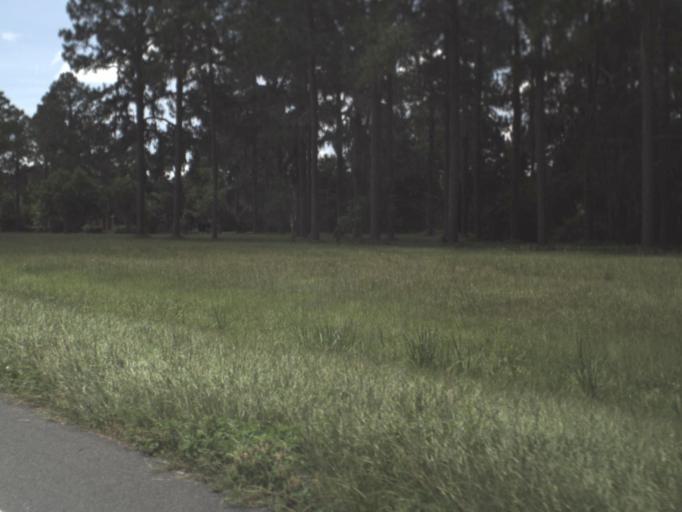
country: US
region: Florida
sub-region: Suwannee County
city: Wellborn
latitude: 30.3907
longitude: -82.8255
